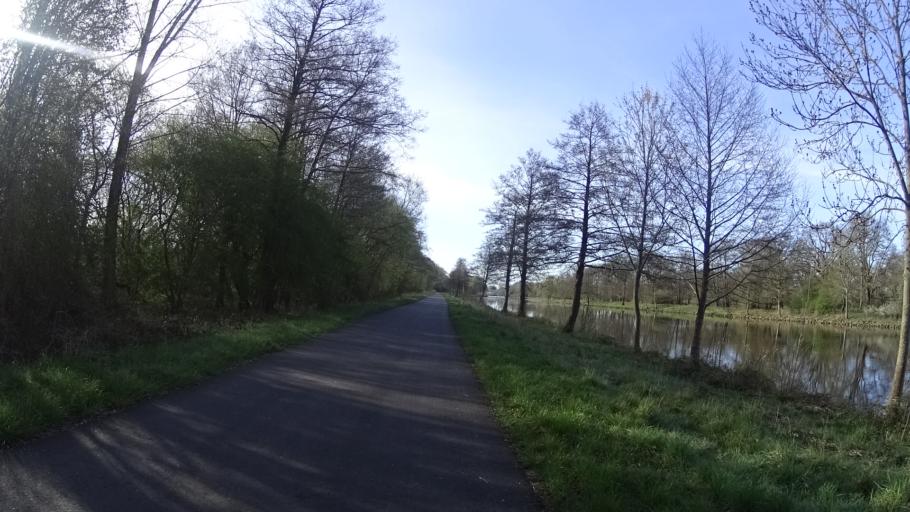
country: DE
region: Lower Saxony
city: Haren
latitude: 52.8031
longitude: 7.2607
